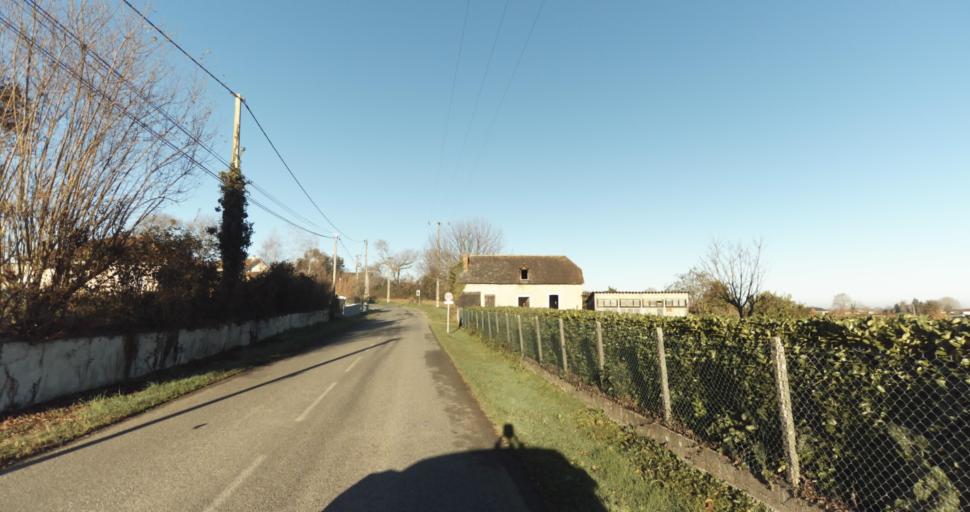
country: FR
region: Aquitaine
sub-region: Departement des Pyrenees-Atlantiques
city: Morlaas
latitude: 43.3224
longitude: -0.2522
